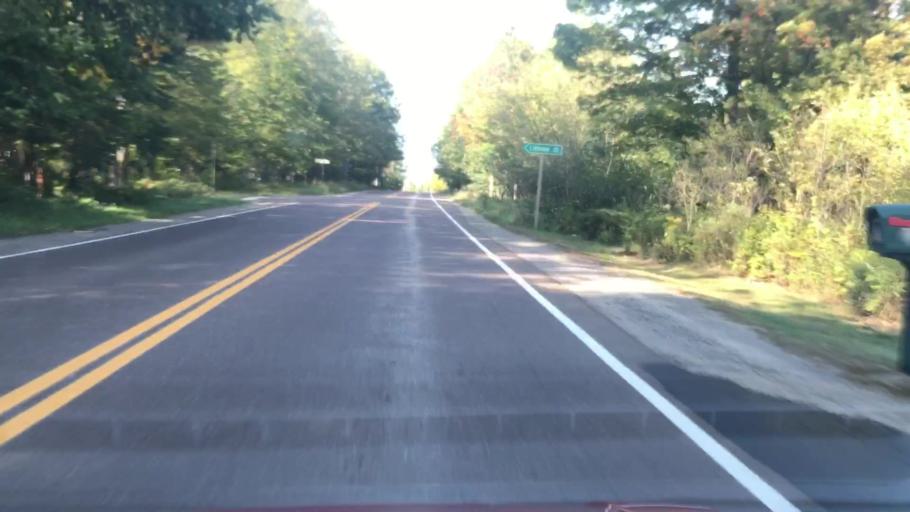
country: US
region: Michigan
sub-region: Chippewa County
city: Sault Ste. Marie
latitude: 46.2819
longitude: -84.0322
